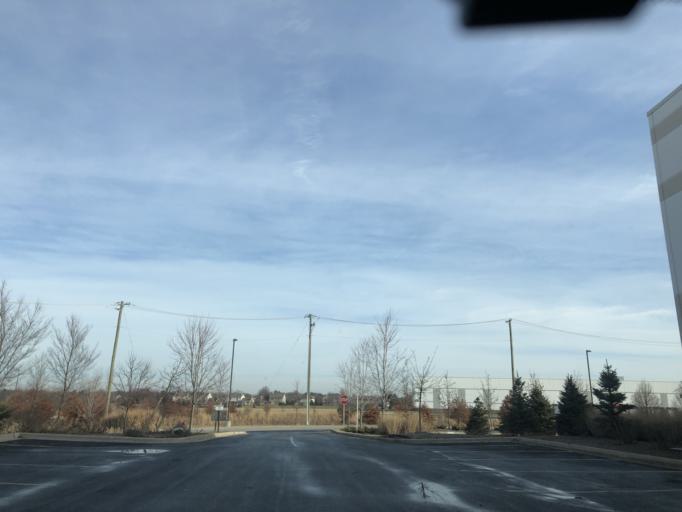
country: US
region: Illinois
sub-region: DuPage County
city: Woodridge
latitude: 41.7174
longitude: -88.0314
